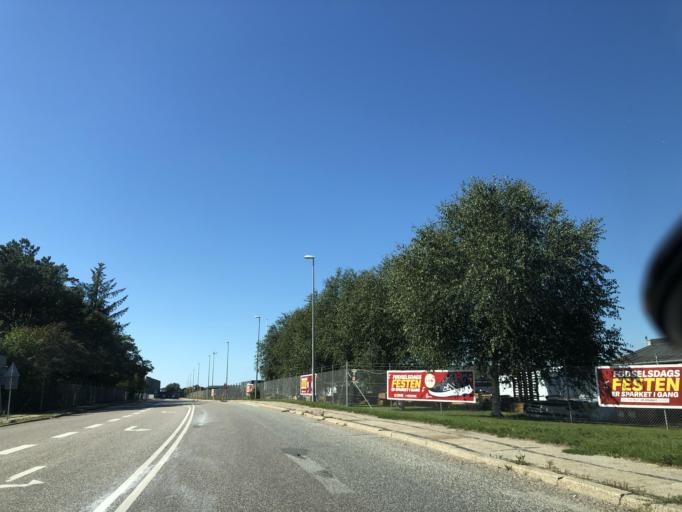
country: DK
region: North Denmark
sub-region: Mariagerfjord Kommune
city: Hobro
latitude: 56.6496
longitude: 9.8024
